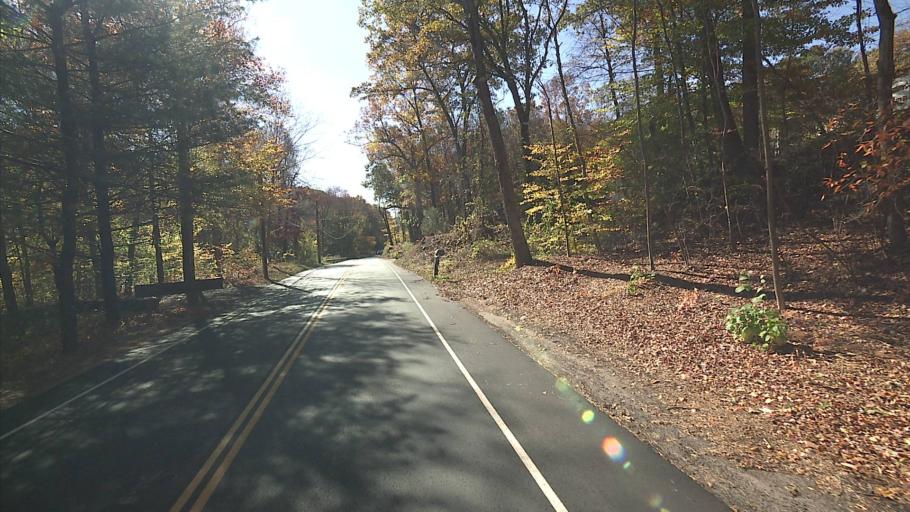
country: US
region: Connecticut
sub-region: Litchfield County
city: Watertown
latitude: 41.6167
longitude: -73.1108
